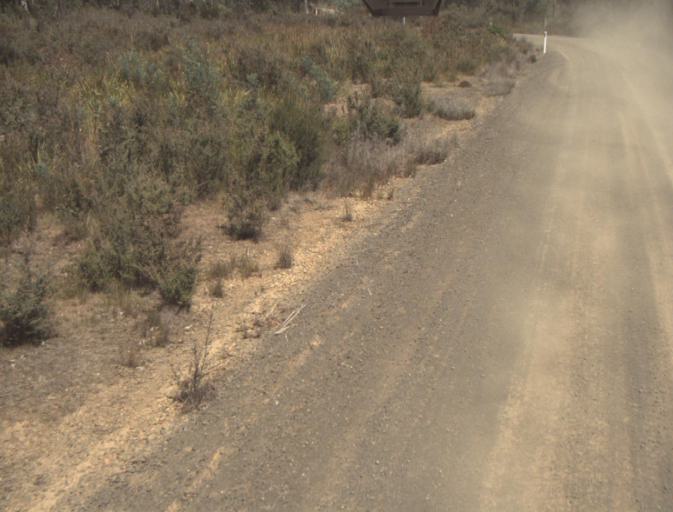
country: AU
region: Tasmania
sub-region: Launceston
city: Mayfield
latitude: -41.2790
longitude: 147.0965
